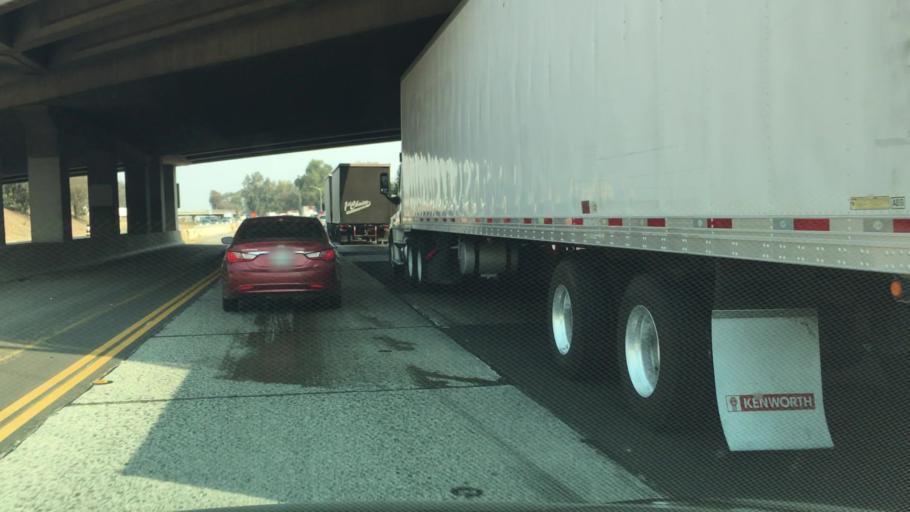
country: US
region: California
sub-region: Fresno County
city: West Park
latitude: 36.7938
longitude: -119.8658
